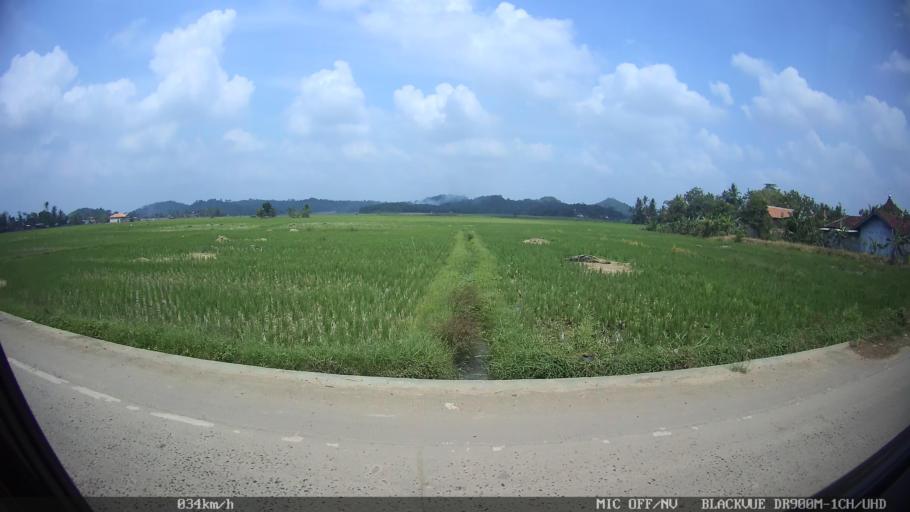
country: ID
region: Lampung
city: Pringsewu
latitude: -5.3716
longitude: 104.9662
